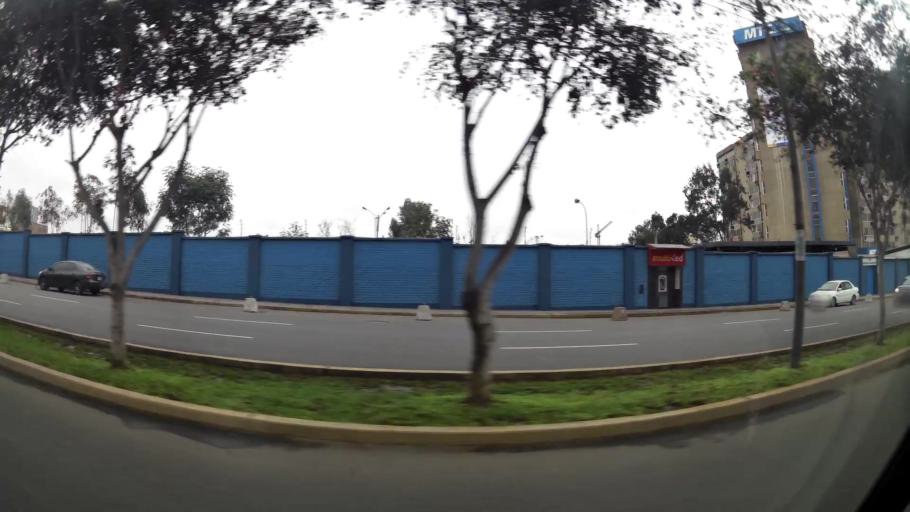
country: PE
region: Lima
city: Lima
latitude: -12.0491
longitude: -77.0553
